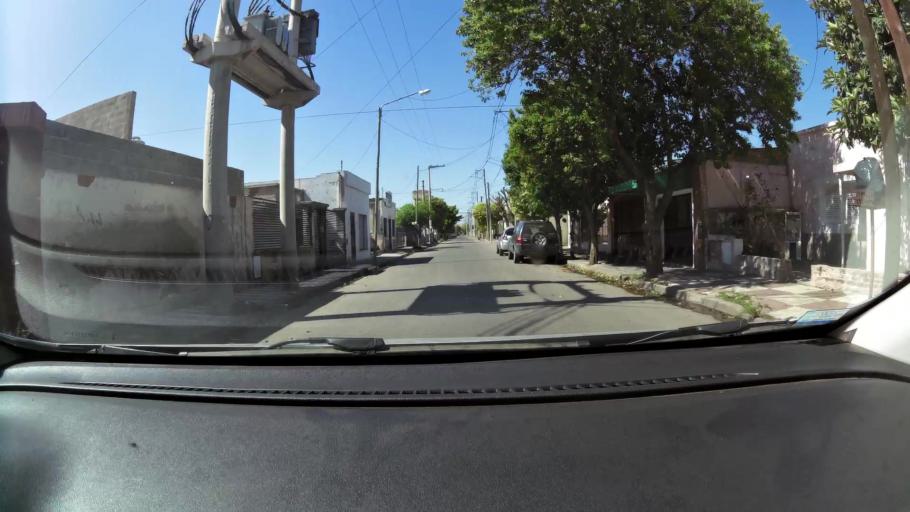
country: AR
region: Cordoba
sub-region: Departamento de Capital
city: Cordoba
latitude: -31.4370
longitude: -64.1356
